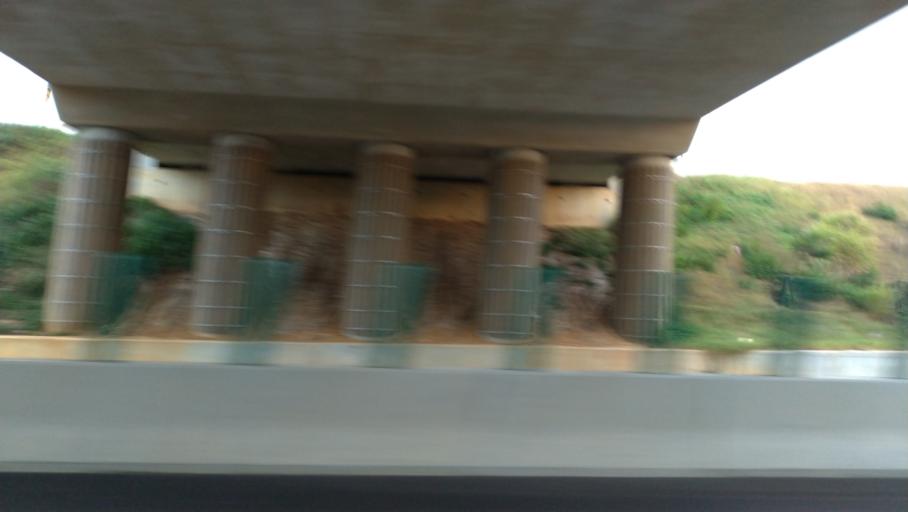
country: TW
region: Taiwan
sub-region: Miaoli
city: Miaoli
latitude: 24.5427
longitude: 120.7015
